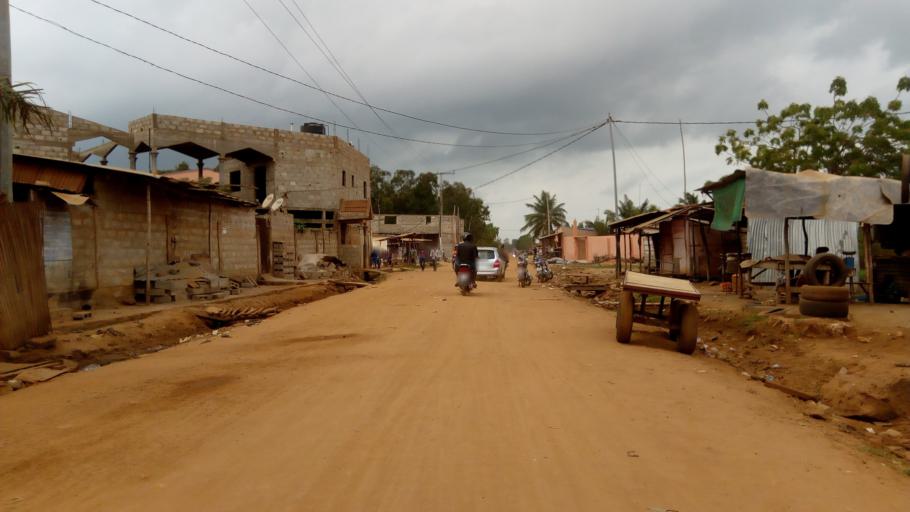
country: TG
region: Maritime
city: Lome
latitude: 6.2551
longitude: 1.2179
